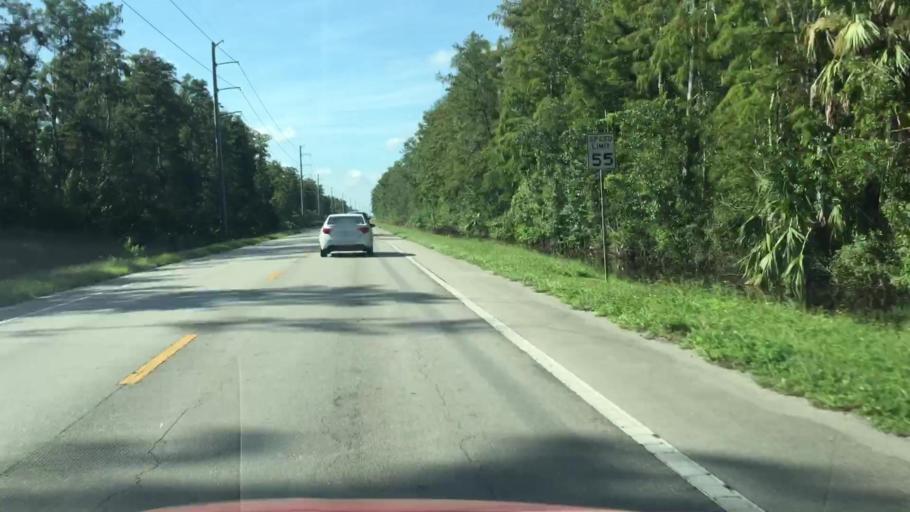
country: US
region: Florida
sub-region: Collier County
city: Orangetree
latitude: 26.3422
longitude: -81.5951
